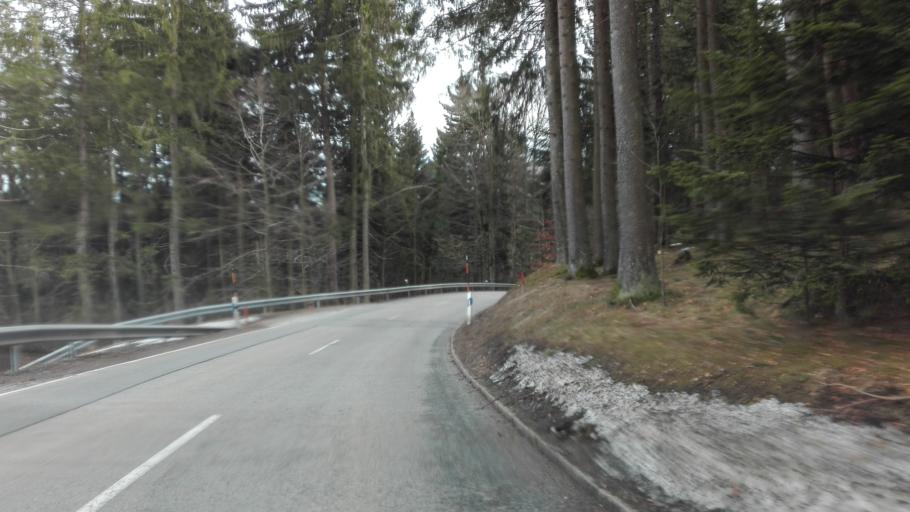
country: DE
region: Bavaria
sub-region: Lower Bavaria
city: Wegscheid
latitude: 48.6321
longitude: 13.7629
